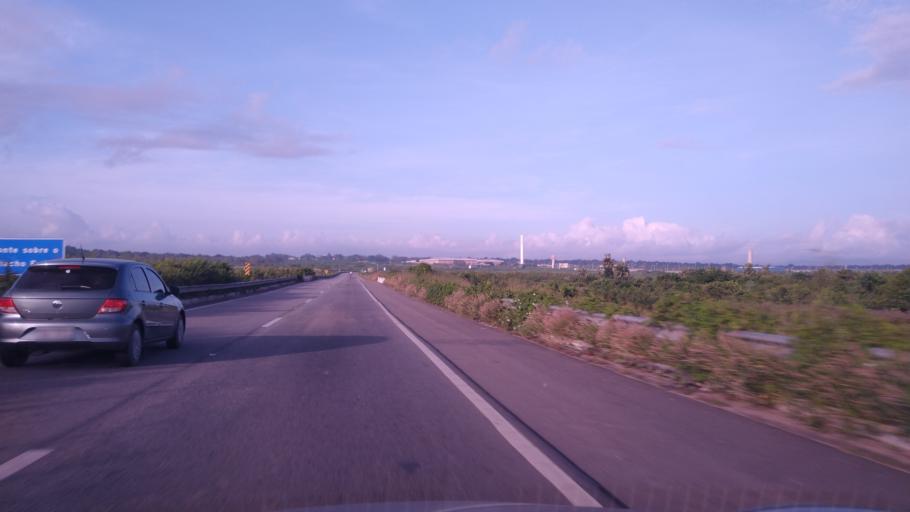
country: BR
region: Ceara
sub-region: Pacajus
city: Pacajus
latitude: -4.1566
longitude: -38.4822
